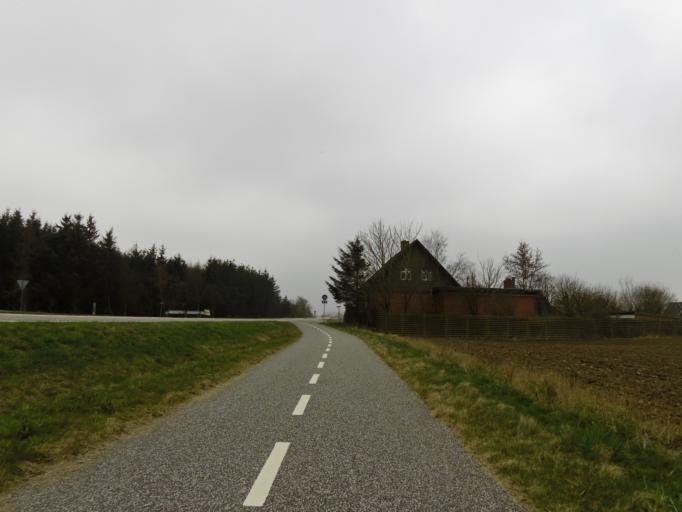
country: DK
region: Central Jutland
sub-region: Holstebro Kommune
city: Vinderup
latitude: 56.4966
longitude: 8.7916
